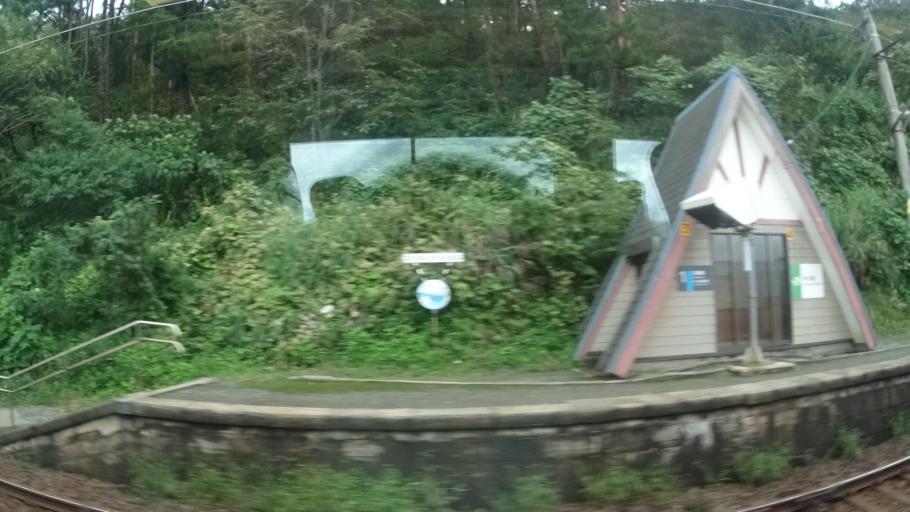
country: JP
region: Niigata
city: Murakami
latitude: 38.4105
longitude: 139.4685
